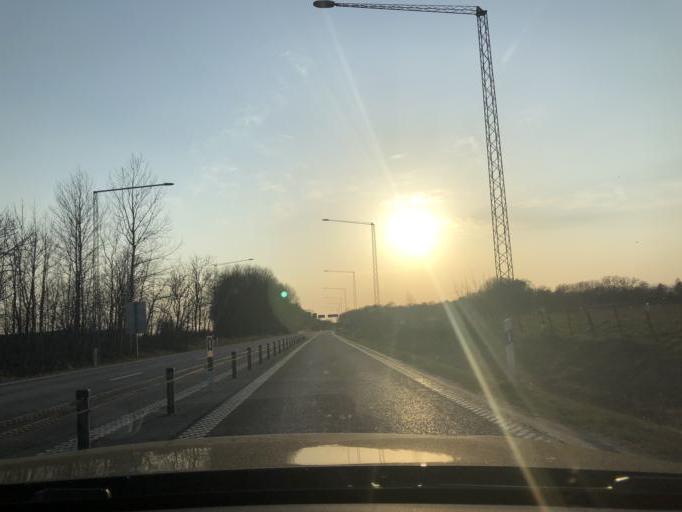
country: SE
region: Kalmar
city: Faerjestaden
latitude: 56.6664
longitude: 16.4945
